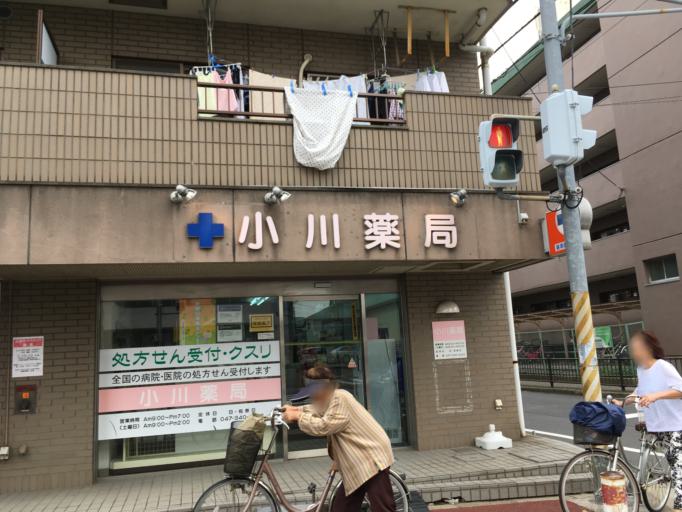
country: JP
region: Chiba
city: Matsudo
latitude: 35.8134
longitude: 139.9114
